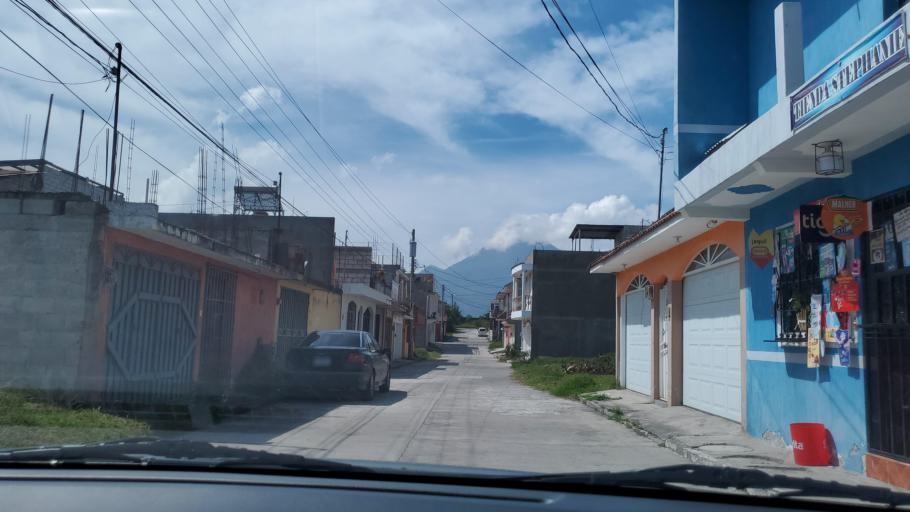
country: GT
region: Quetzaltenango
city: Quetzaltenango
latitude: 14.8313
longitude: -91.5399
